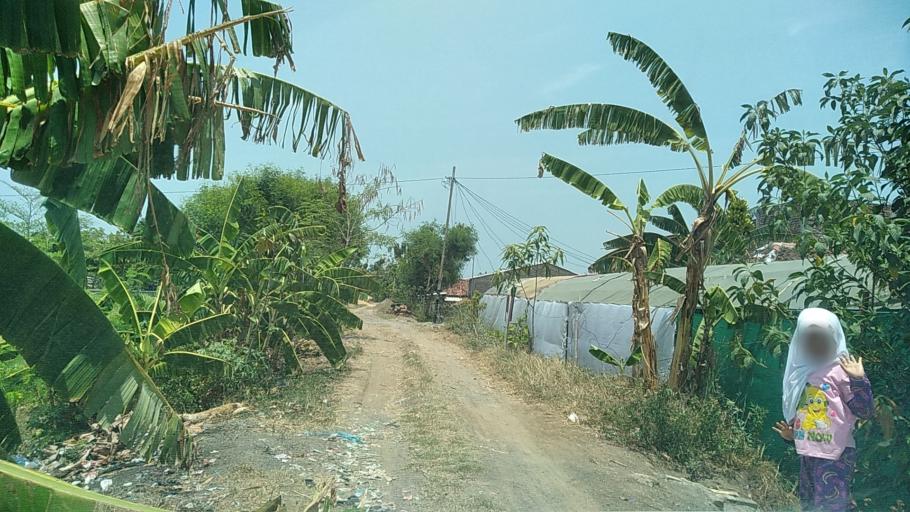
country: ID
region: Central Java
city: Mranggen
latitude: -6.9561
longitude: 110.4917
